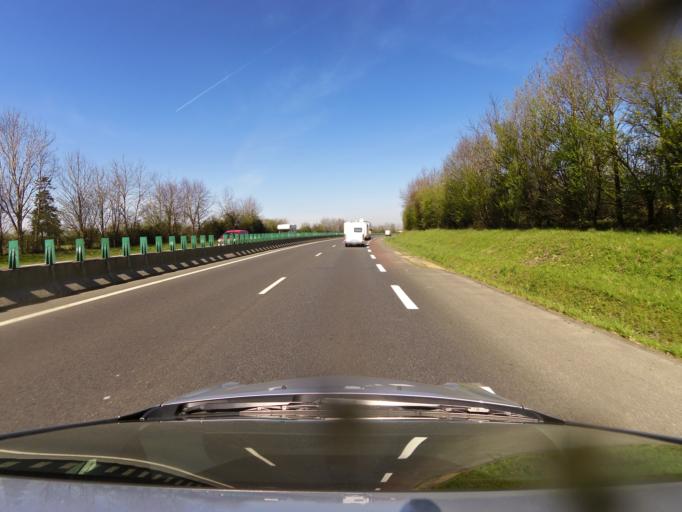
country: FR
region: Lower Normandy
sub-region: Departement de la Manche
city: Le Val-Saint-Pere
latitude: 48.6584
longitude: -1.3621
